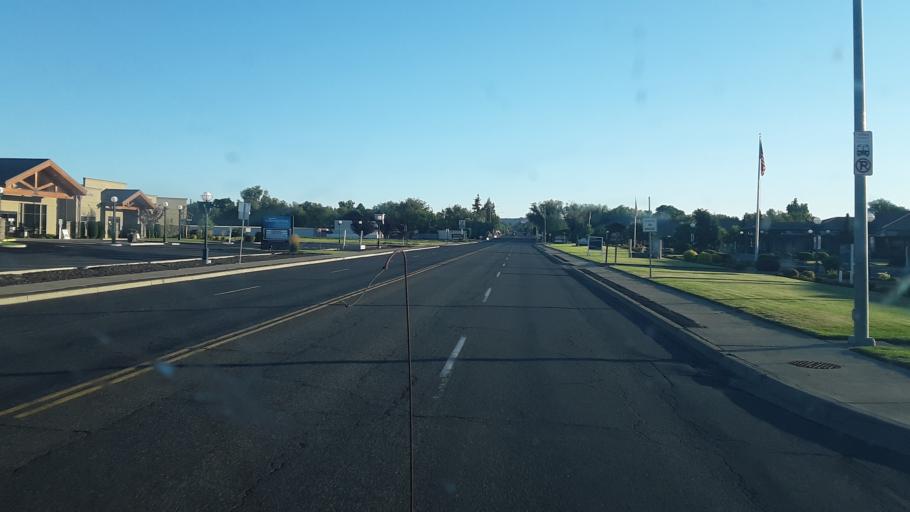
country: US
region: Washington
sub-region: Yakima County
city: West Valley
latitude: 46.5761
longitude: -120.5620
